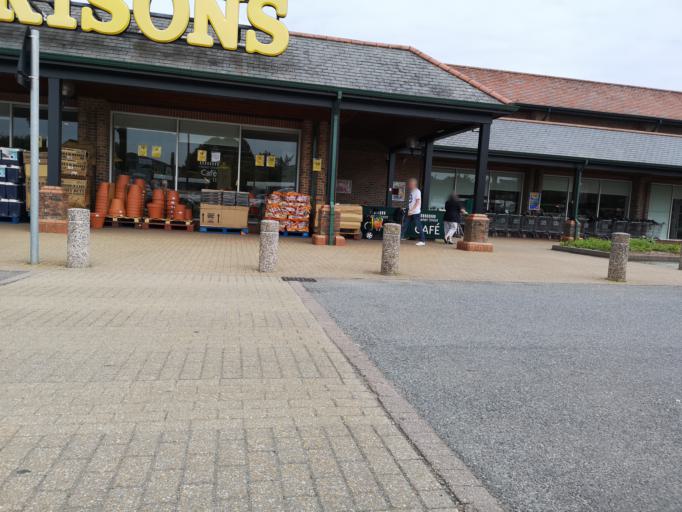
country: GB
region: England
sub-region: Isle of Wight
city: Shanklin
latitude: 50.6466
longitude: -1.1813
